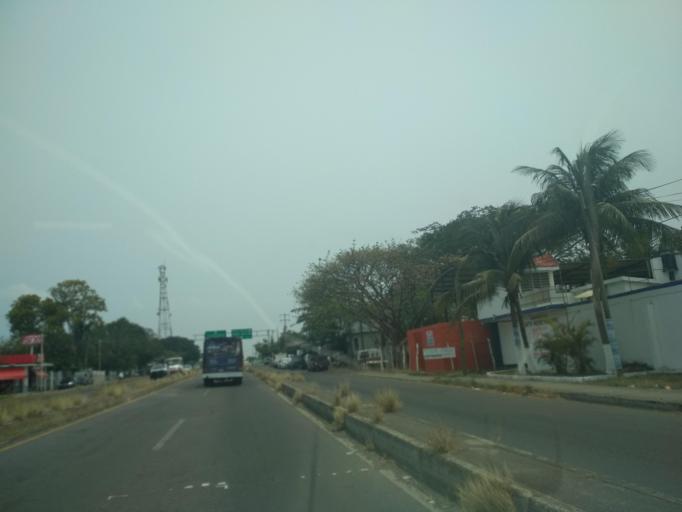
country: MX
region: Veracruz
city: Paso del Toro
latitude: 19.0315
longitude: -96.1378
